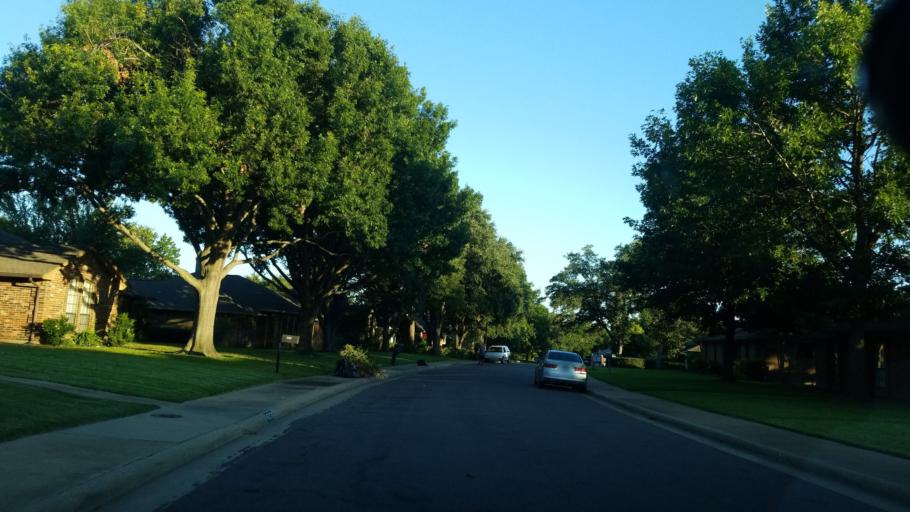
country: US
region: Texas
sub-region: Dallas County
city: Balch Springs
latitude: 32.7873
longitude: -96.6956
